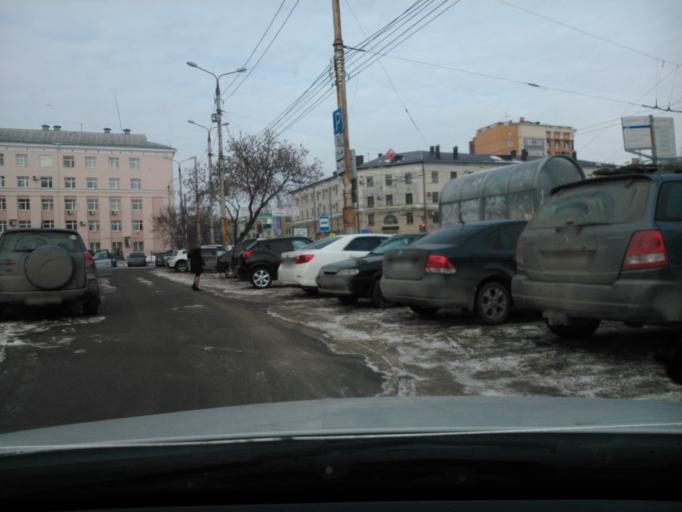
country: RU
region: Perm
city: Perm
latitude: 57.9932
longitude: 56.2478
